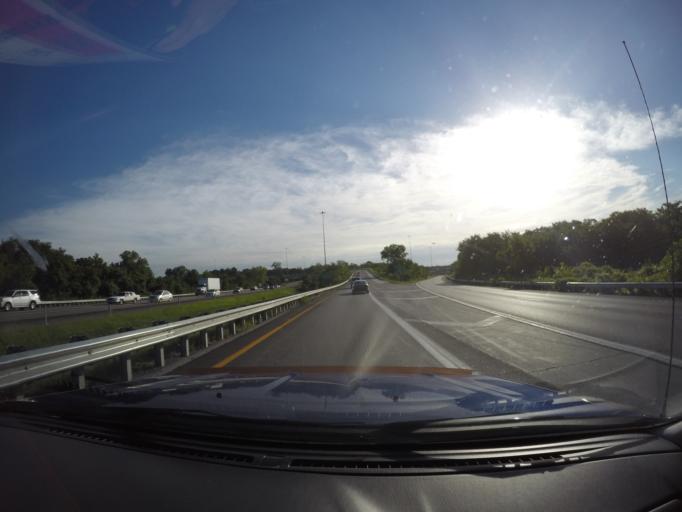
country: US
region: Missouri
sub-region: Platte County
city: Riverside
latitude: 39.1883
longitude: -94.6187
